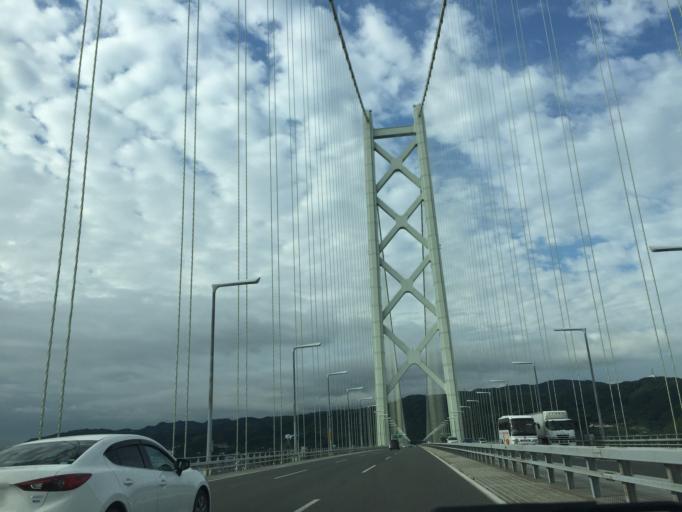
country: JP
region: Hyogo
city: Akashi
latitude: 34.6122
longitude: 135.0172
